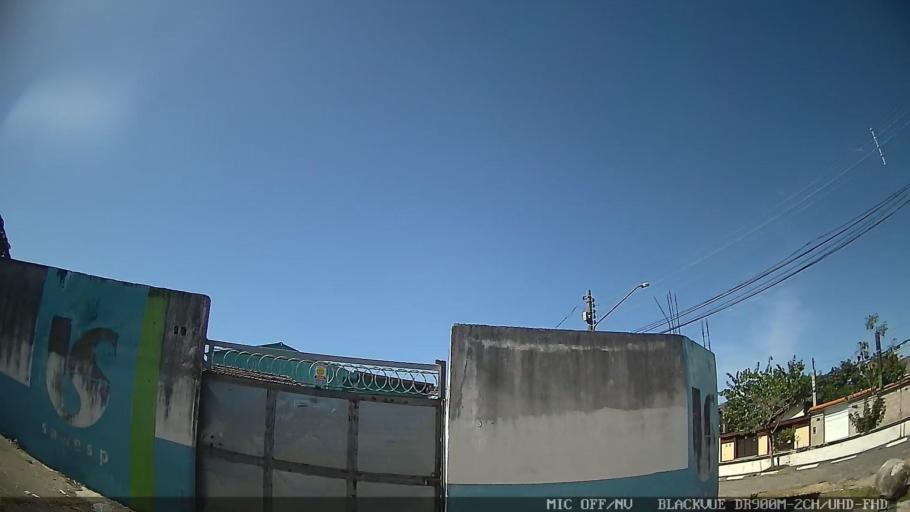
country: BR
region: Sao Paulo
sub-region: Guaruja
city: Guaruja
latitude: -23.9656
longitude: -46.2788
